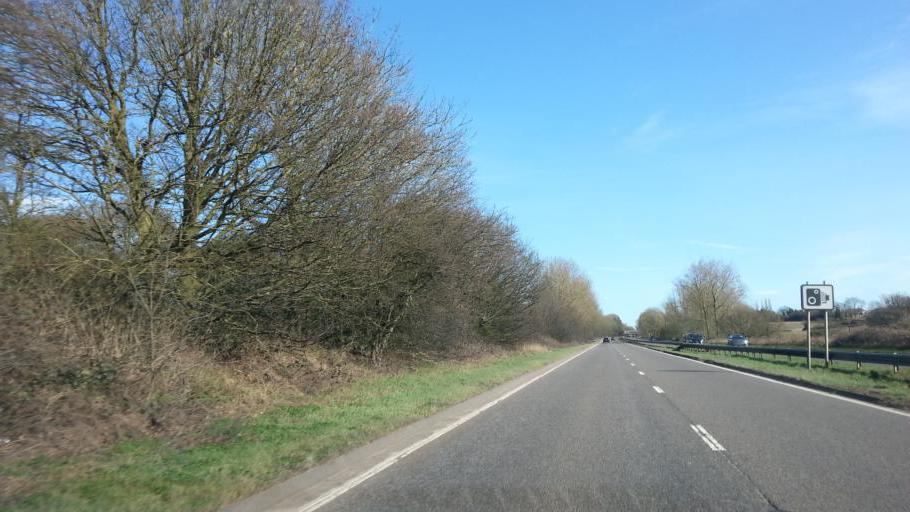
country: GB
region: England
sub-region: Solihull
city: Meriden
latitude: 52.4407
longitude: -1.6288
